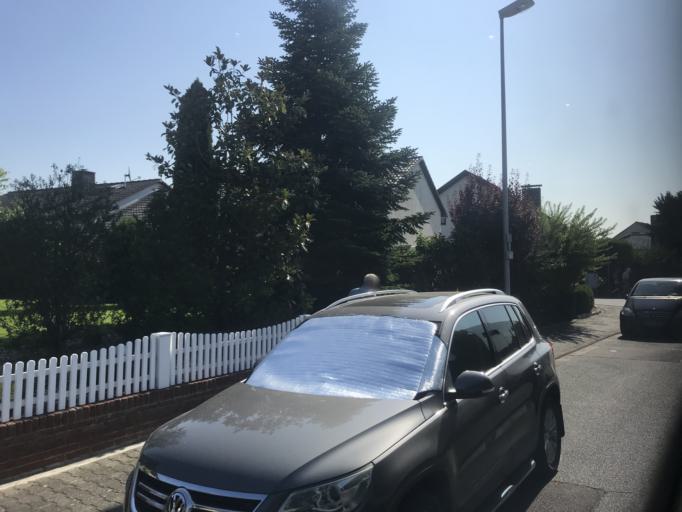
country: DE
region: Hesse
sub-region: Regierungsbezirk Darmstadt
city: Ginsheim-Gustavsburg
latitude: 49.9893
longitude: 8.3479
